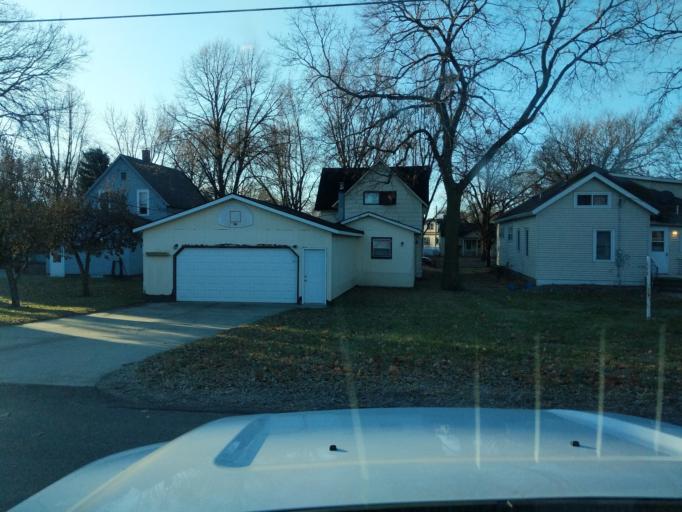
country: US
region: Minnesota
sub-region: Yellow Medicine County
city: Granite Falls
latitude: 44.8083
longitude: -95.5426
